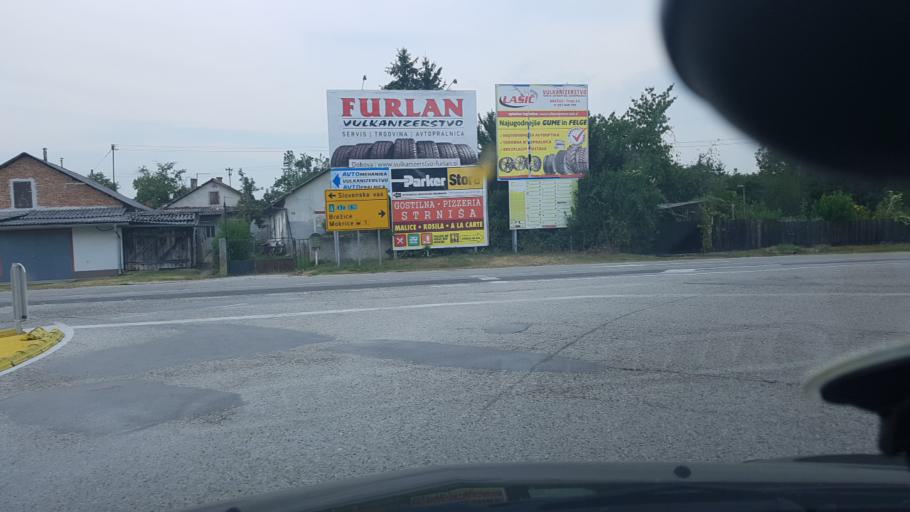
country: HR
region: Zagrebacka
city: Bregana
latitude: 45.8433
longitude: 15.6835
